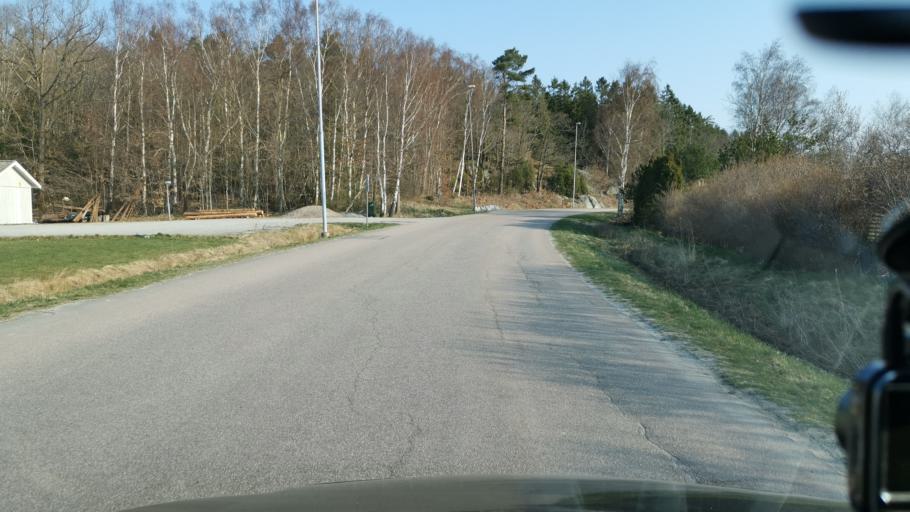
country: SE
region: Vaestra Goetaland
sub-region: Kungalvs Kommun
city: Kode
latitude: 57.9434
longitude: 11.8363
